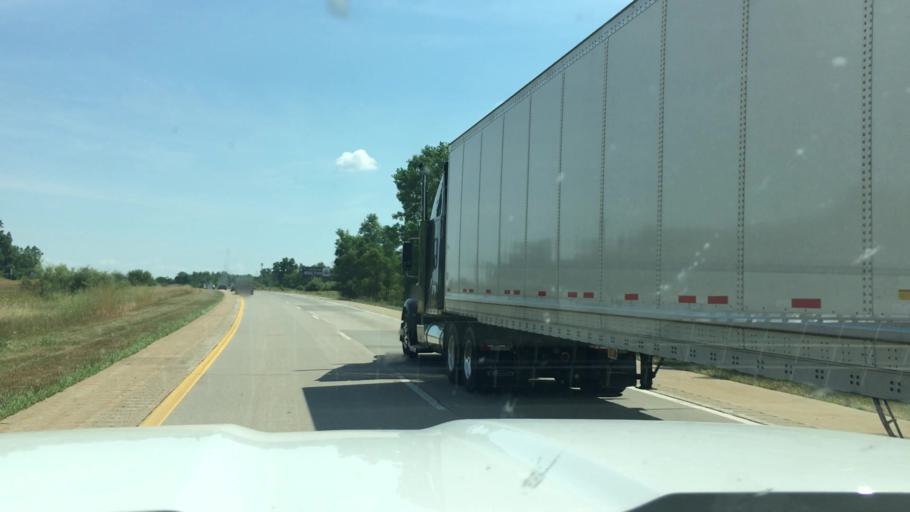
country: US
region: Michigan
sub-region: Ingham County
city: Haslett
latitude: 42.7829
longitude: -84.3858
